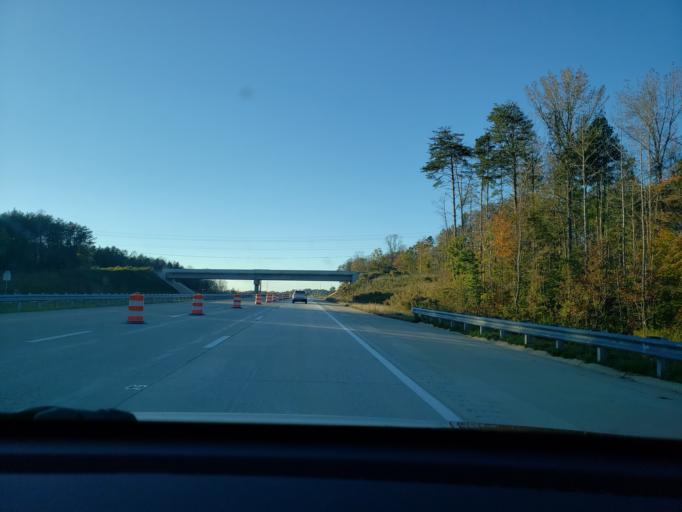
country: US
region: North Carolina
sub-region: Forsyth County
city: Walkertown
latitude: 36.1404
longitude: -80.1446
